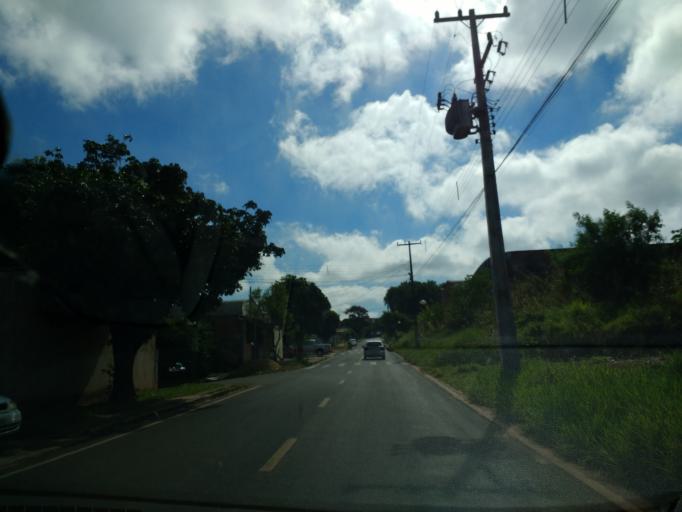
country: BR
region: Parana
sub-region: Umuarama
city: Umuarama
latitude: -23.7764
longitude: -53.3000
